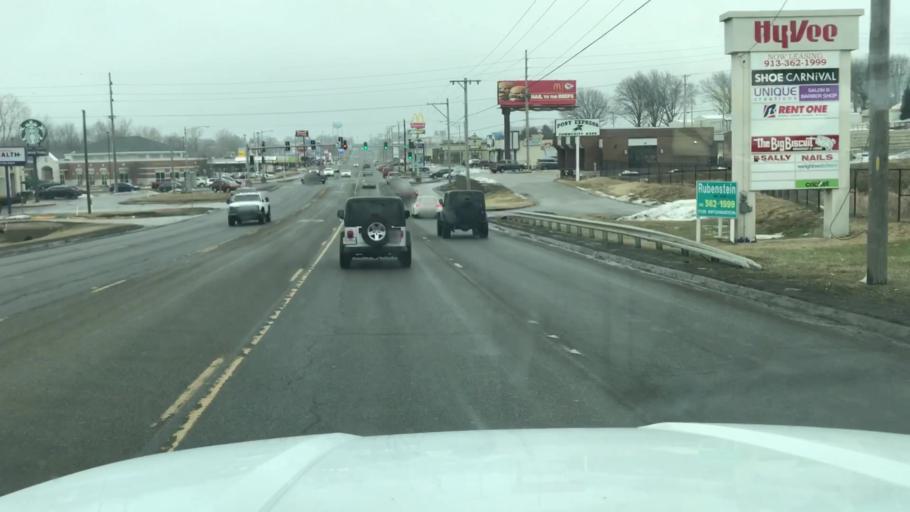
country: US
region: Missouri
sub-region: Buchanan County
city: Saint Joseph
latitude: 39.7684
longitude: -94.8035
